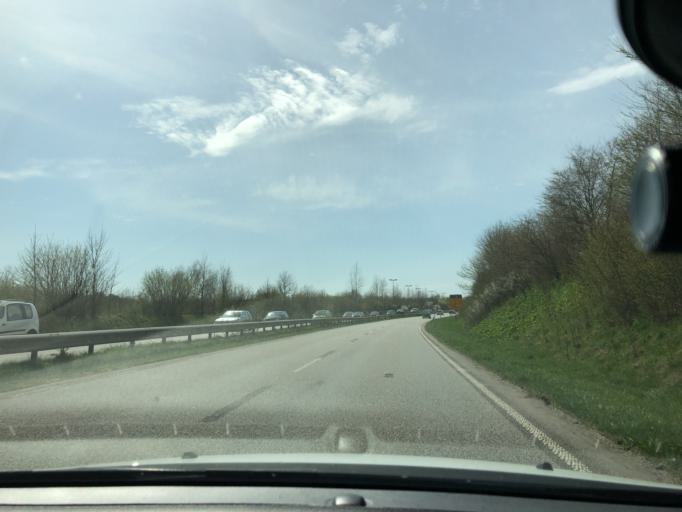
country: DE
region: Schleswig-Holstein
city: Flensburg
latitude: 54.7628
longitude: 9.4552
